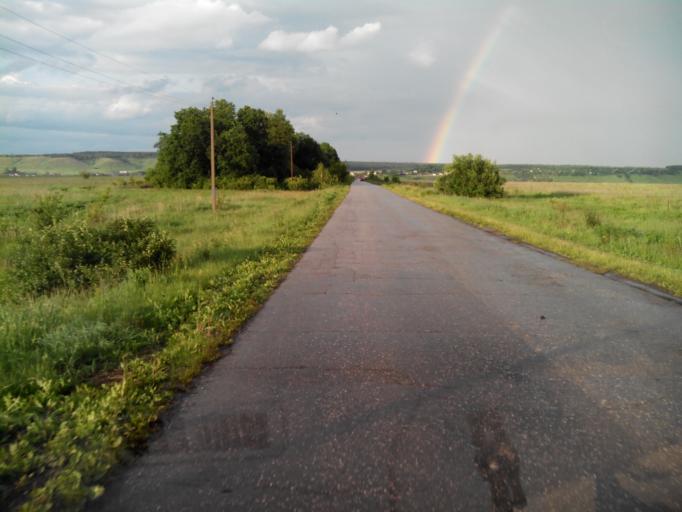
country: RU
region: Penza
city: Zasechnoye
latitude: 53.0641
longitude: 44.9945
